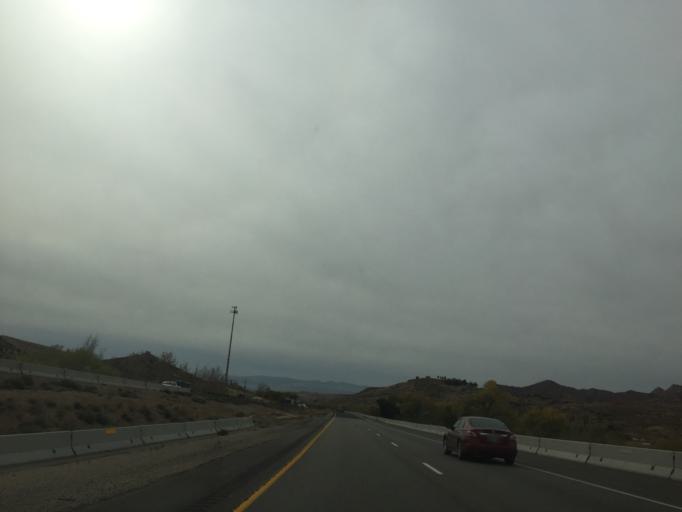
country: US
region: Utah
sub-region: Washington County
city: Toquerville
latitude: 37.2400
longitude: -113.3633
